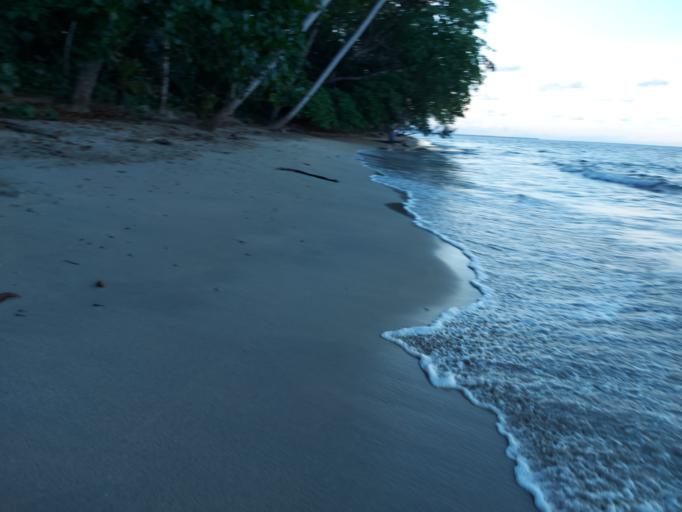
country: PA
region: Bocas del Toro
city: Barranco
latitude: 9.6419
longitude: -82.7124
